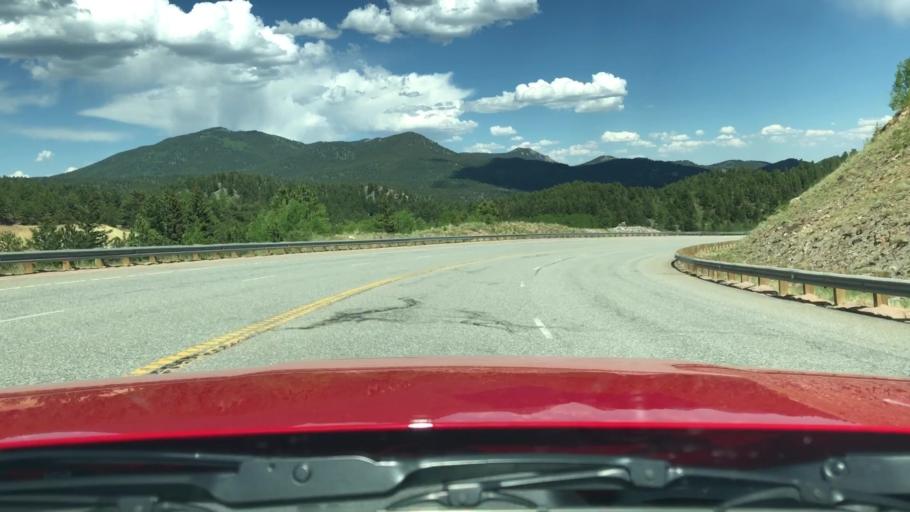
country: US
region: Colorado
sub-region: Gilpin County
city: Central City
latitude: 39.7863
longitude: -105.4879
